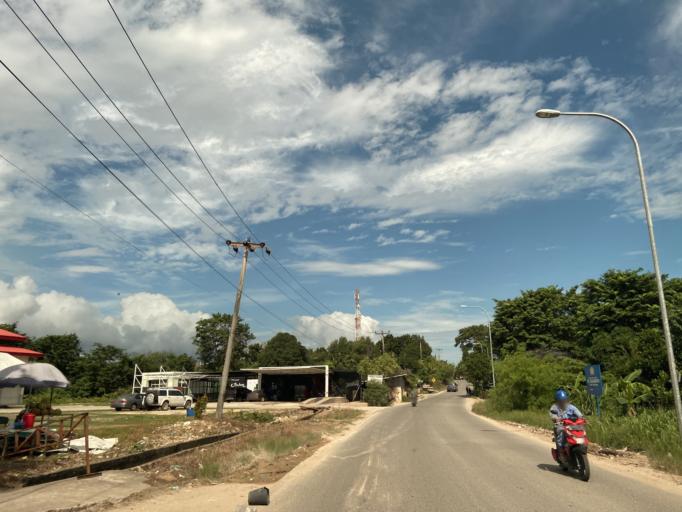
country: SG
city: Singapore
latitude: 1.0341
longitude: 103.9391
